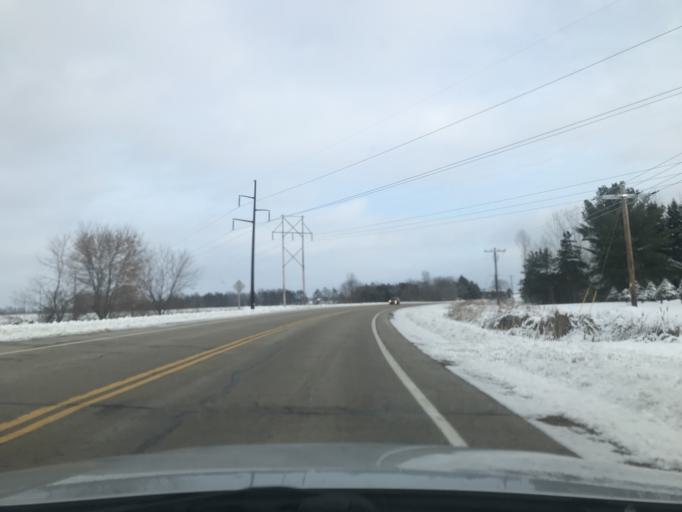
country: US
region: Wisconsin
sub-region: Oconto County
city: Oconto
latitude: 44.8933
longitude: -87.9991
